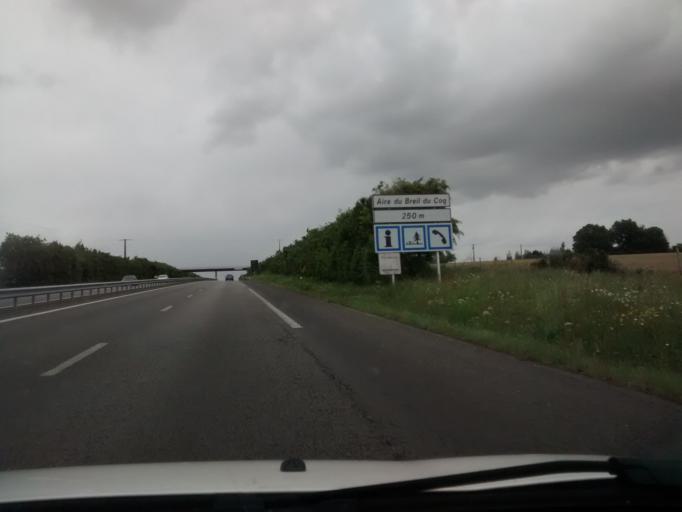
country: FR
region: Brittany
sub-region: Departement d'Ille-et-Vilaine
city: Plelan-le-Grand
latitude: 47.9667
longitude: -2.0945
